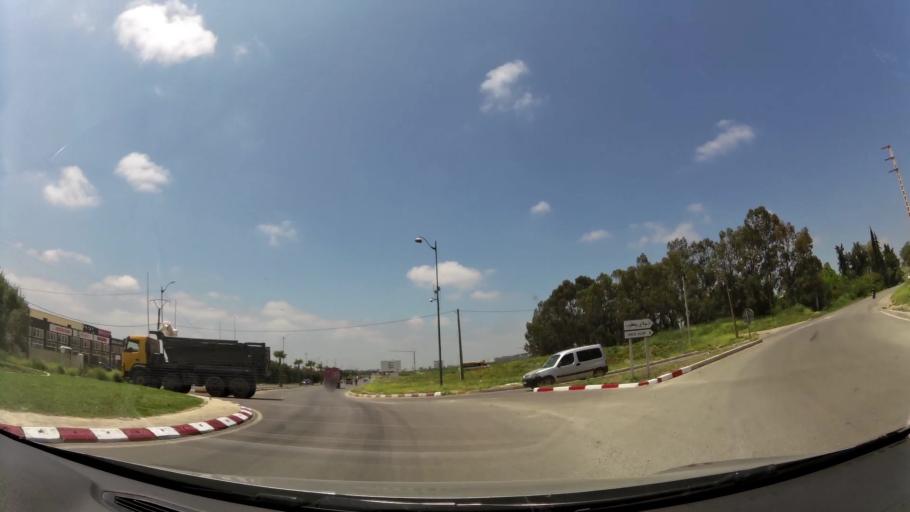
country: MA
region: Fes-Boulemane
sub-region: Fes
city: Fes
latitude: 34.0454
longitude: -5.0551
